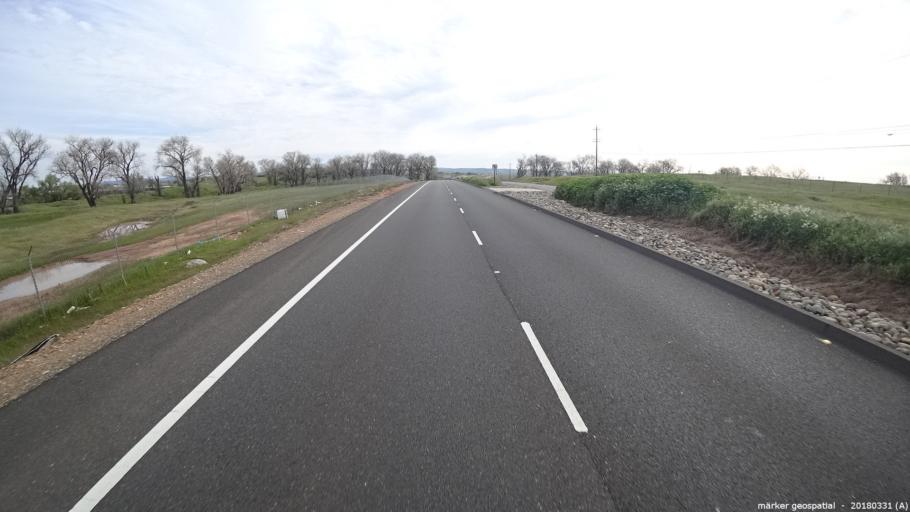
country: US
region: California
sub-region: Sacramento County
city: Folsom
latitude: 38.6102
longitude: -121.1636
